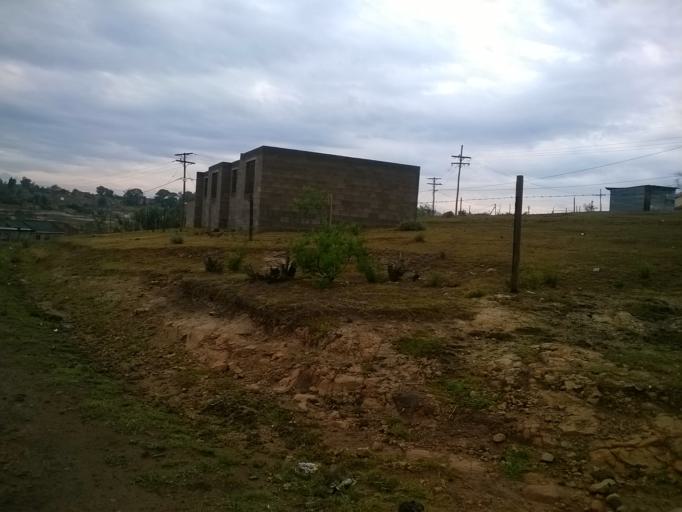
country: LS
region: Berea
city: Teyateyaneng
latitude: -29.1421
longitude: 27.7415
